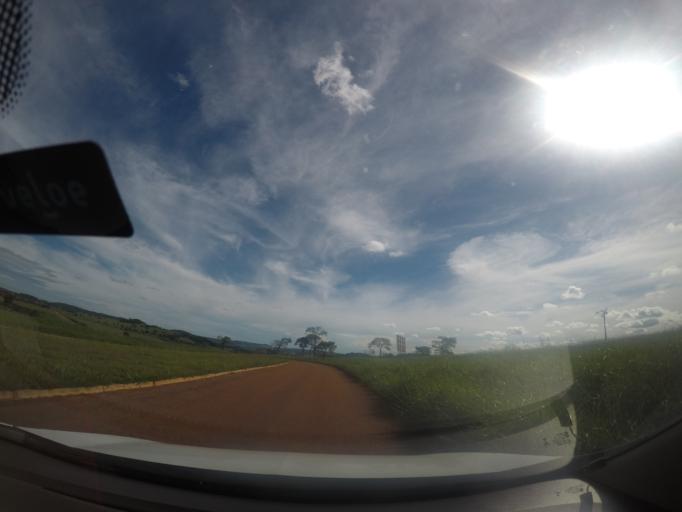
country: BR
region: Goias
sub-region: Inhumas
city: Inhumas
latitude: -16.4081
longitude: -49.4720
